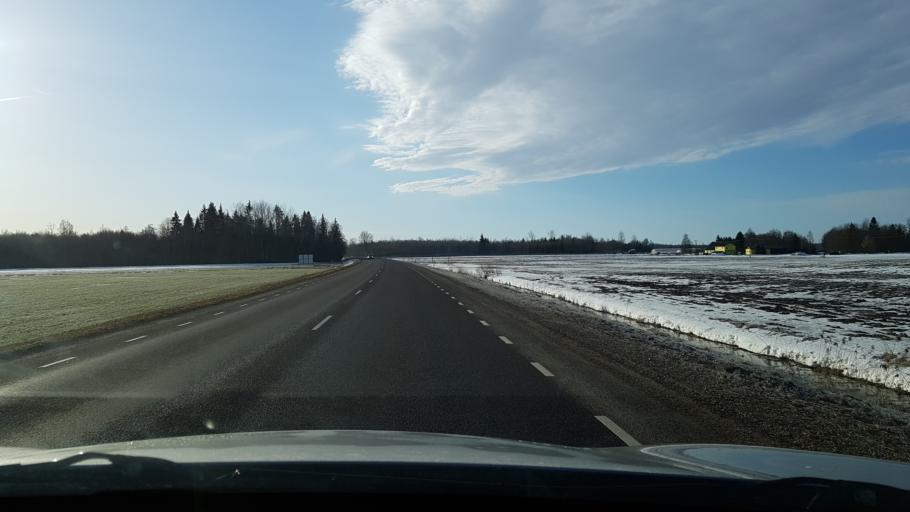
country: EE
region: Viljandimaa
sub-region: Vohma linn
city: Vohma
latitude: 58.6232
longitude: 25.5689
